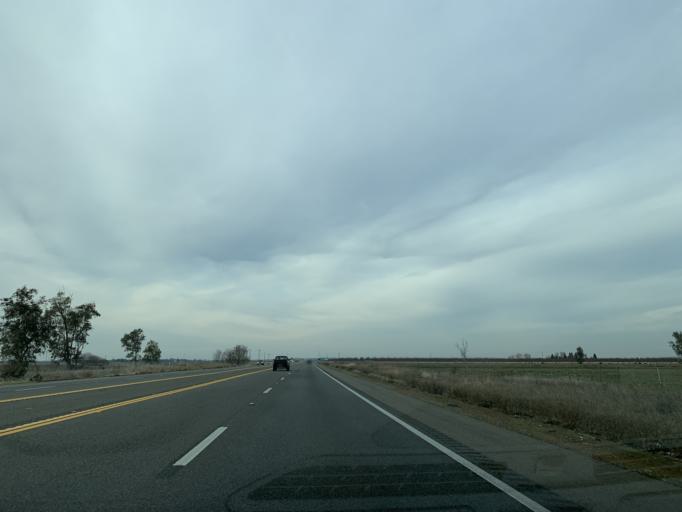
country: US
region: California
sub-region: Yuba County
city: Plumas Lake
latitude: 38.8623
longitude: -121.5513
